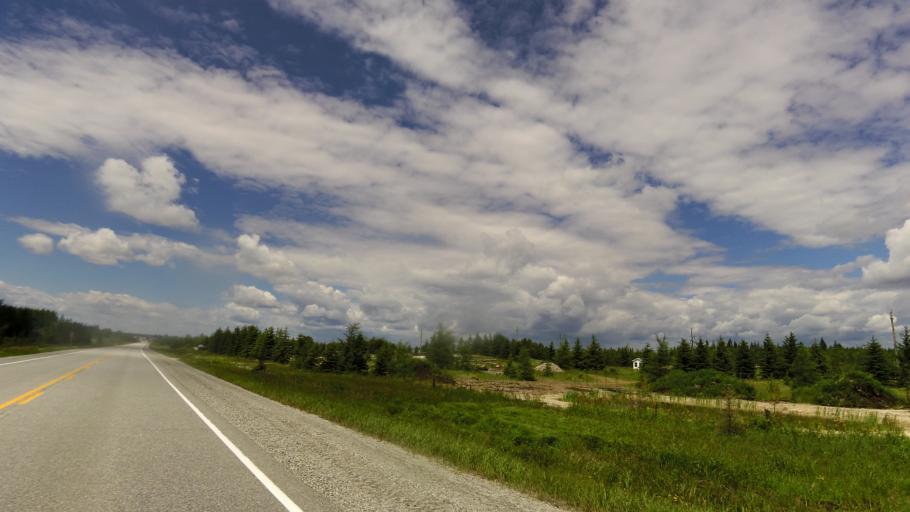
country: CA
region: Ontario
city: Kapuskasing
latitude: 49.3064
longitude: -82.0100
